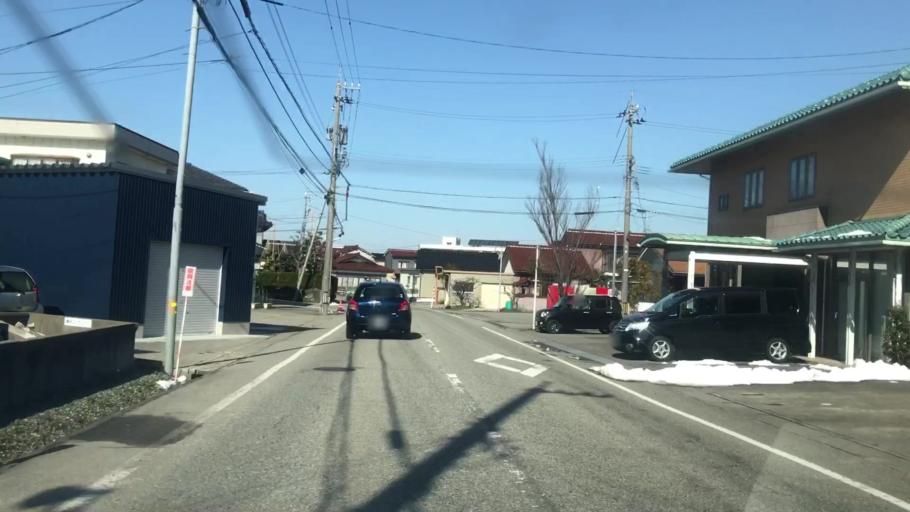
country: JP
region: Toyama
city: Toyama-shi
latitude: 36.6654
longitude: 137.2401
